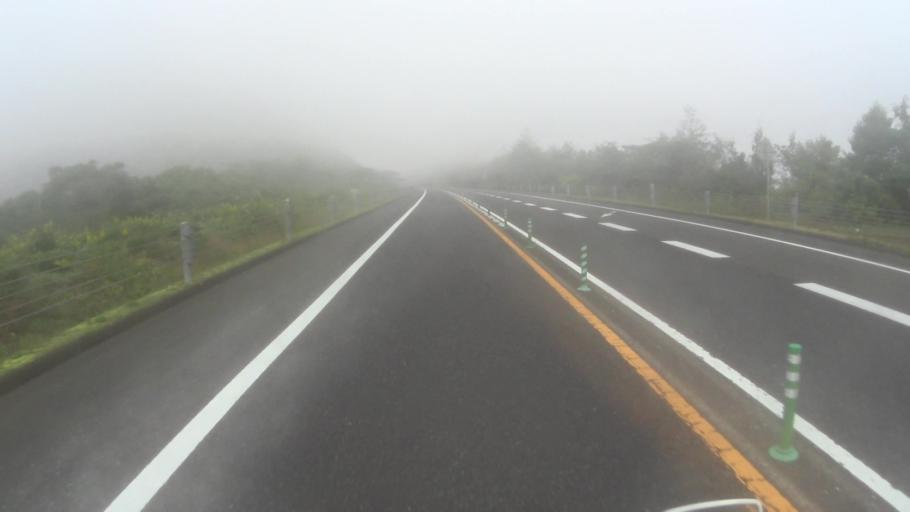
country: JP
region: Kyoto
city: Ayabe
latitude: 35.3804
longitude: 135.2558
